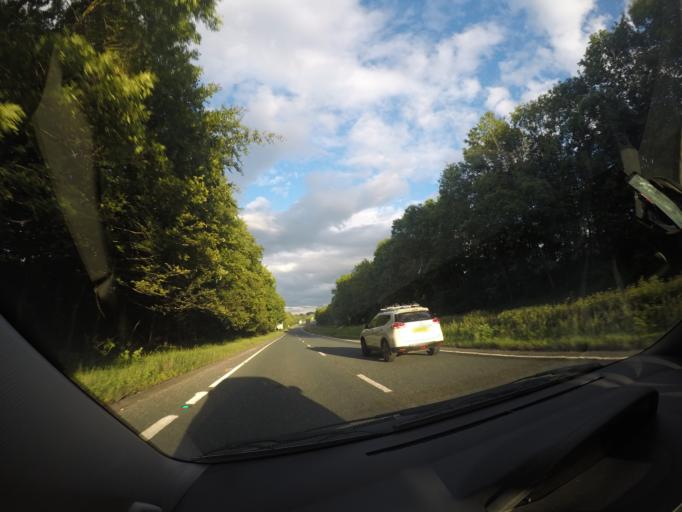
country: GB
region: England
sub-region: County Durham
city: Rokeby
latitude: 54.5174
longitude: -1.8720
